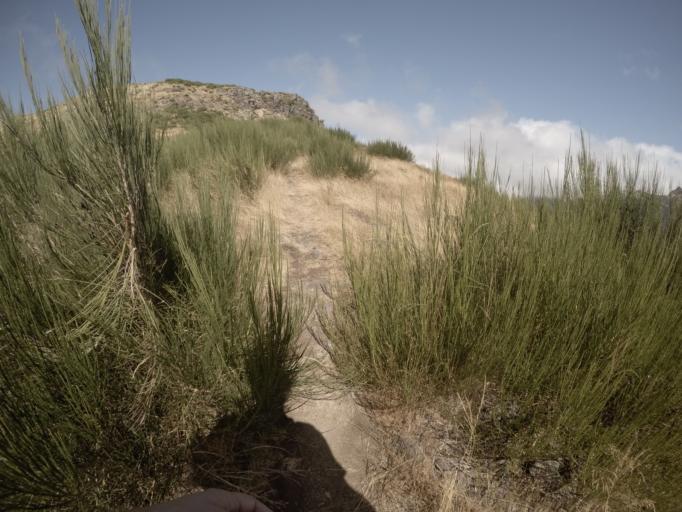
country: PT
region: Madeira
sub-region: Camara de Lobos
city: Curral das Freiras
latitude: 32.7159
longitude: -16.9985
